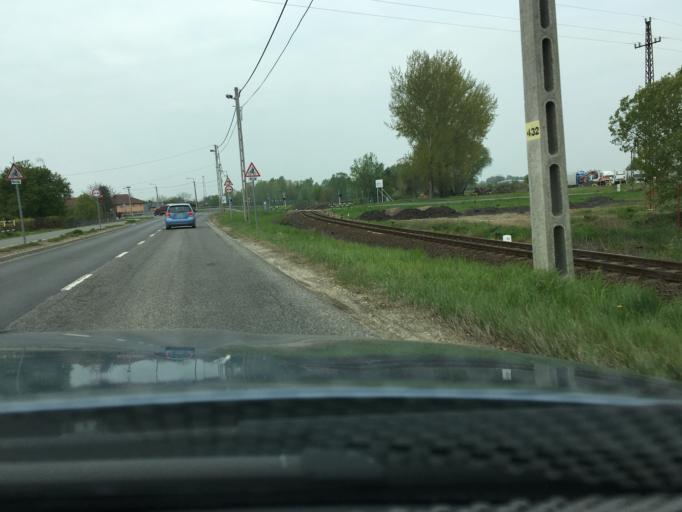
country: HU
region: Hajdu-Bihar
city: Hajdusamson
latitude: 47.6127
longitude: 21.7670
